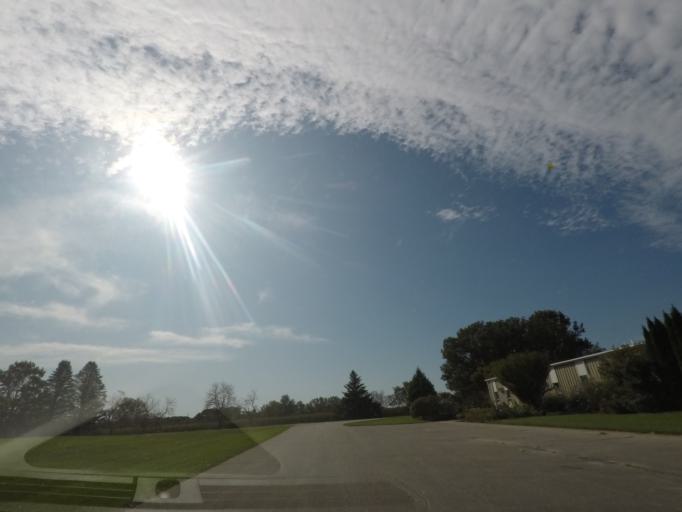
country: US
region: Iowa
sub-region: Story County
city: Gilbert
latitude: 42.1081
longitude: -93.5888
